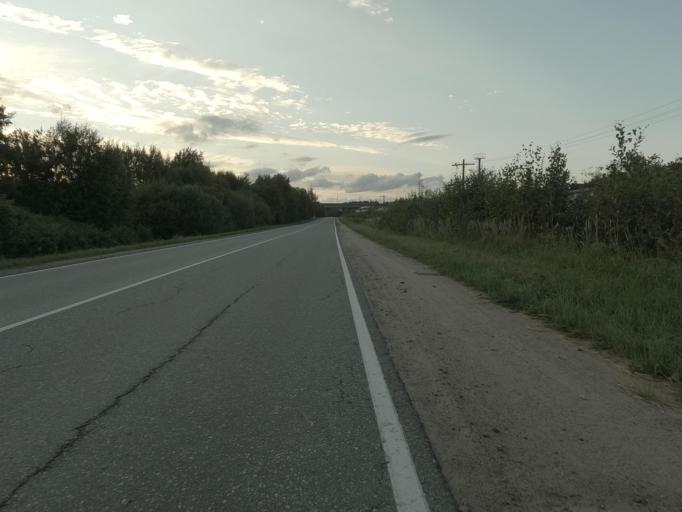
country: RU
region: Leningrad
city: Mga
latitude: 59.7553
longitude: 31.0231
